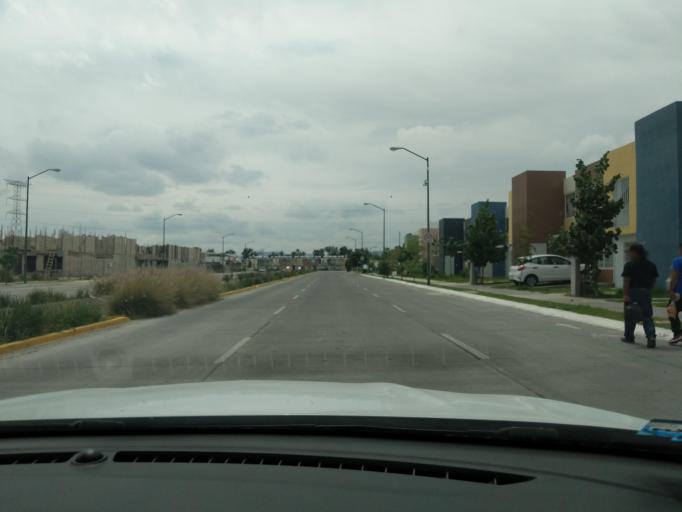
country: MX
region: Jalisco
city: Tesistan
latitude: 20.7879
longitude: -103.4892
